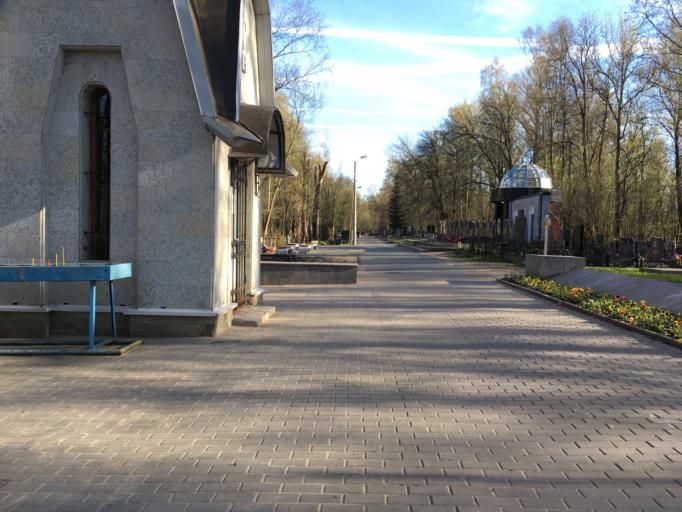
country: RU
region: St.-Petersburg
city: Komendantsky aerodrom
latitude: 59.9981
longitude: 30.2643
